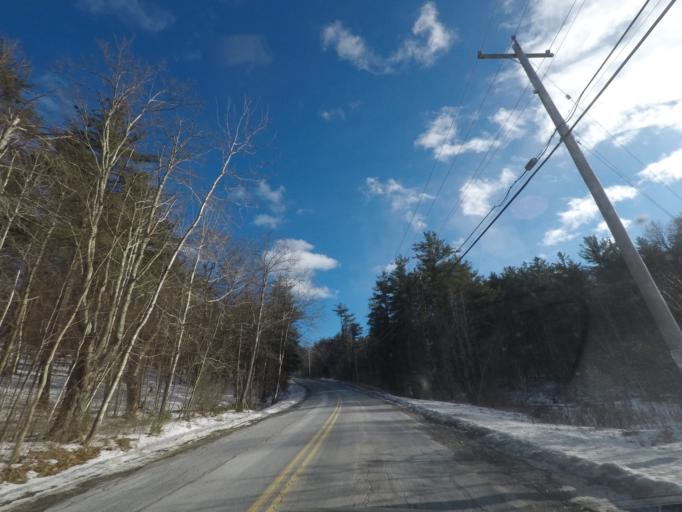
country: US
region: New York
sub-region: Rensselaer County
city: Hoosick Falls
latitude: 42.8277
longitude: -73.3904
